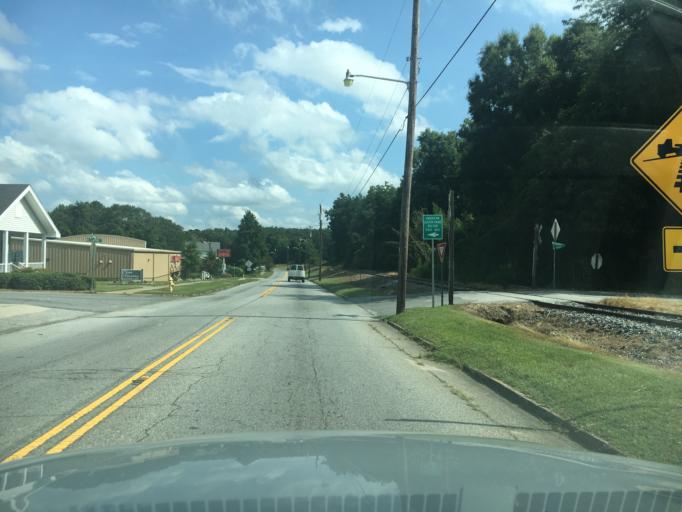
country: US
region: South Carolina
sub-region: Anderson County
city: Belton
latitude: 34.5202
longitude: -82.4922
